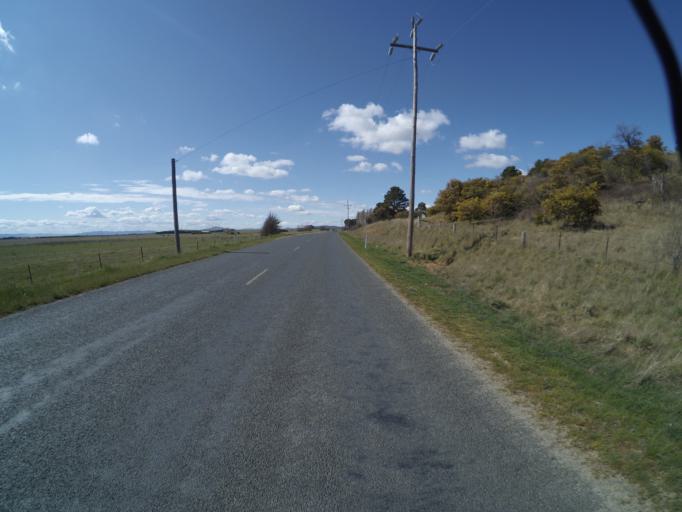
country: AU
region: New South Wales
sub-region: Palerang
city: Bungendore
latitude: -35.2308
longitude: 149.4476
